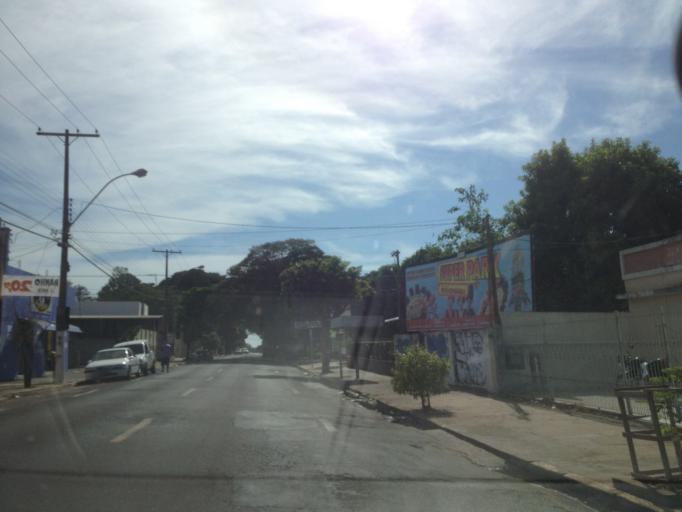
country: BR
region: Sao Paulo
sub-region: Marilia
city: Marilia
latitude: -22.2079
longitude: -49.9355
